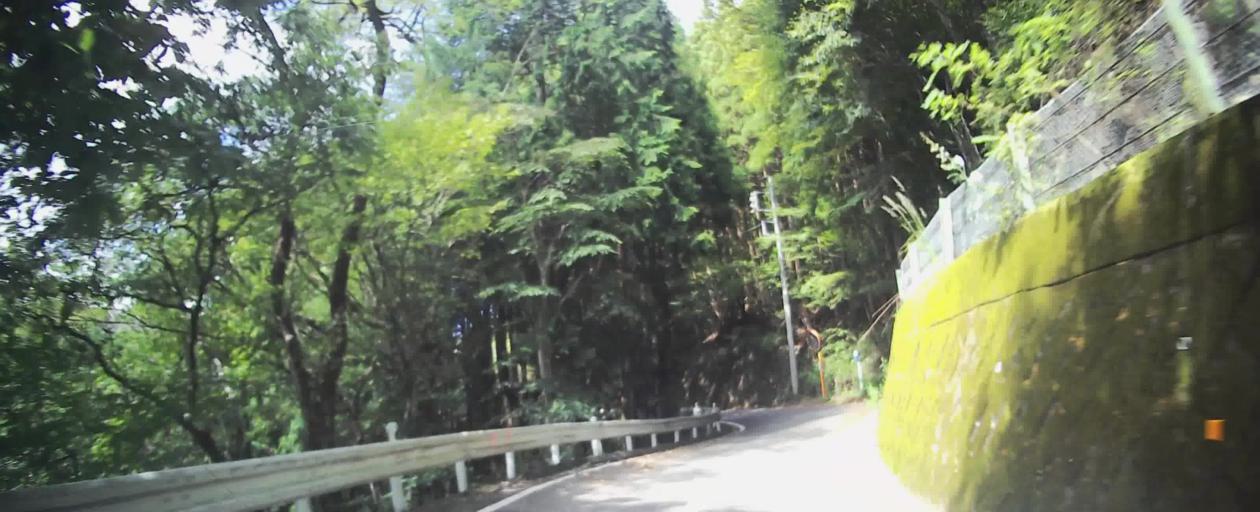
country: JP
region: Gunma
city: Kanekomachi
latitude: 36.4470
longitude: 138.9054
